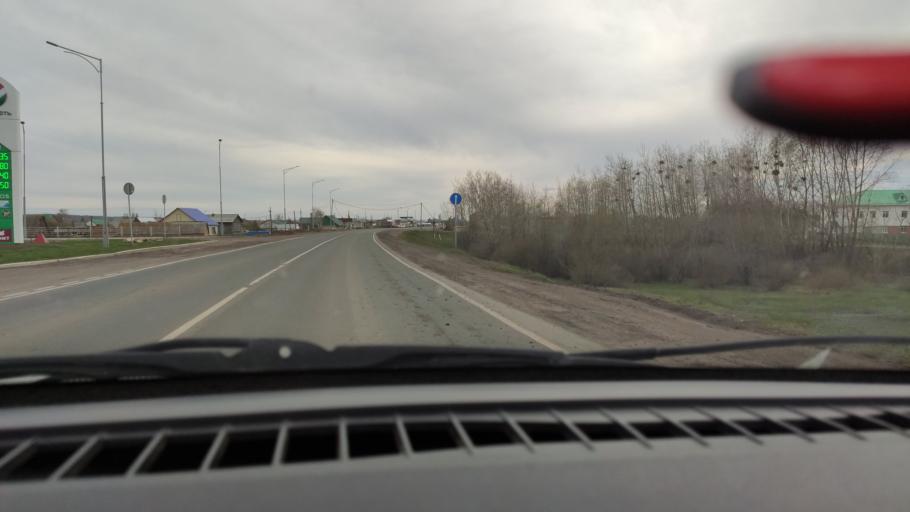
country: RU
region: Bashkortostan
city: Mayachnyy
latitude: 52.4281
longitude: 55.7878
